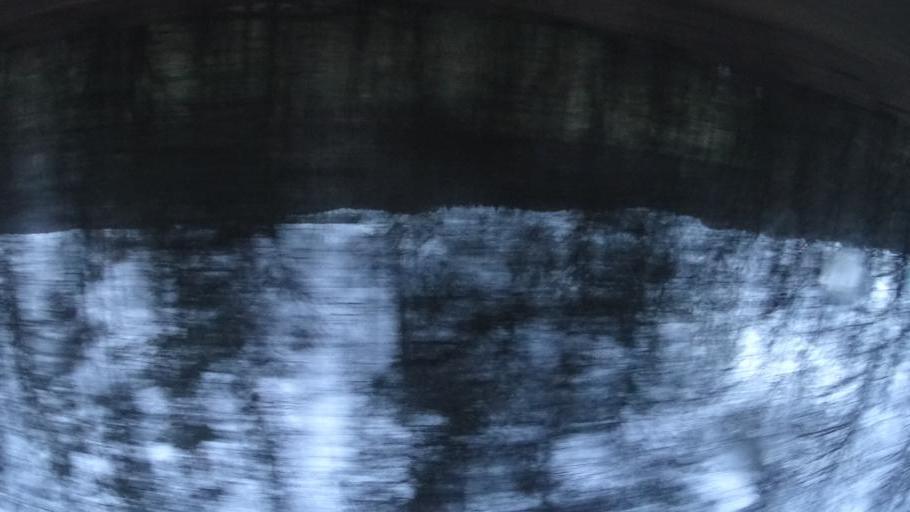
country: DE
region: Hesse
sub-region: Regierungsbezirk Kassel
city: Eichenzell
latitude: 50.4558
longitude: 9.7218
